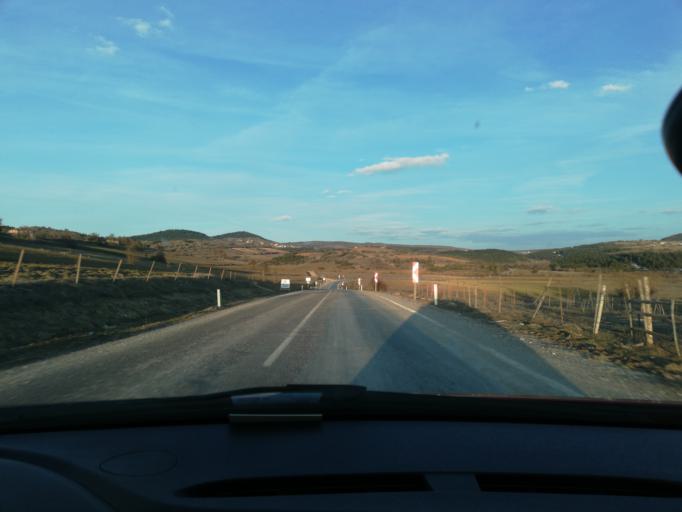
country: TR
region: Kastamonu
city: Agli
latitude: 41.6943
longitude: 33.6063
